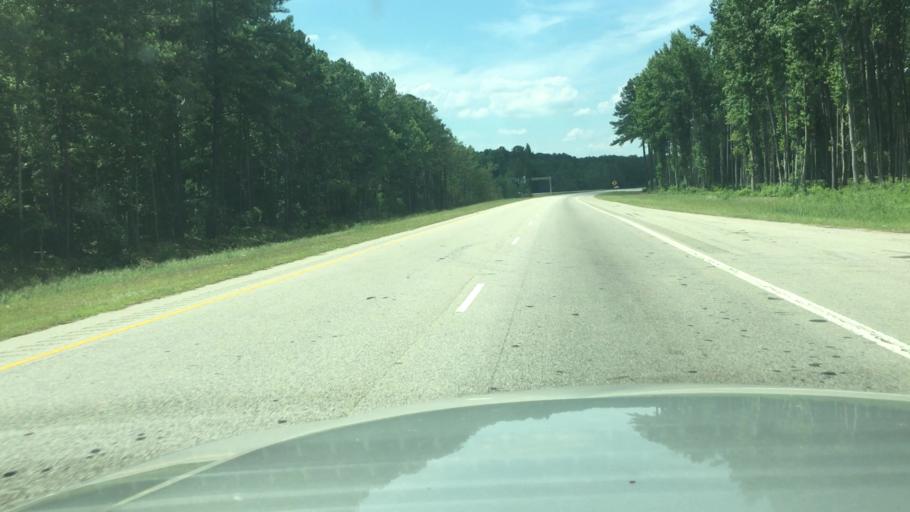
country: US
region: North Carolina
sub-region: Cumberland County
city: Fayetteville
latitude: 34.9785
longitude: -78.8573
